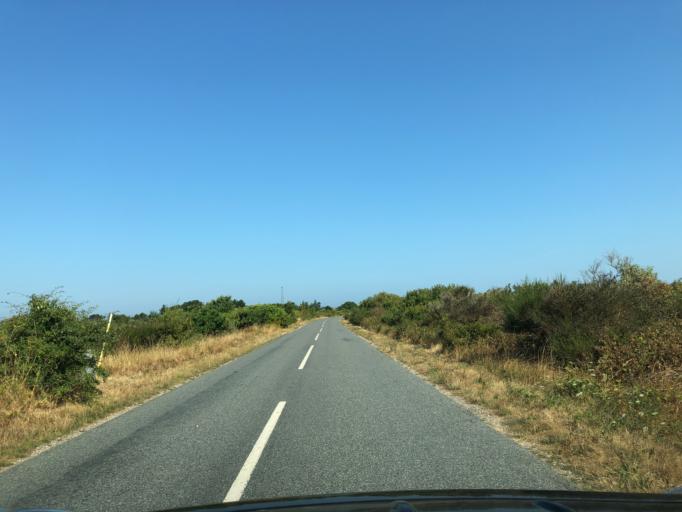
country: DK
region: Zealand
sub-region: Odsherred Kommune
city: Asnaes
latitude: 55.9963
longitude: 11.2898
